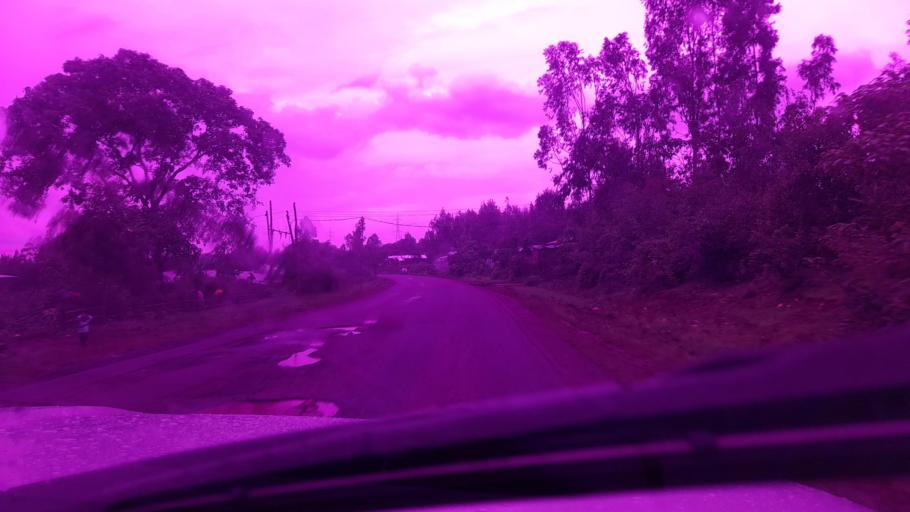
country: ET
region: Oromiya
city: Jima
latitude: 7.7089
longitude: 37.0277
